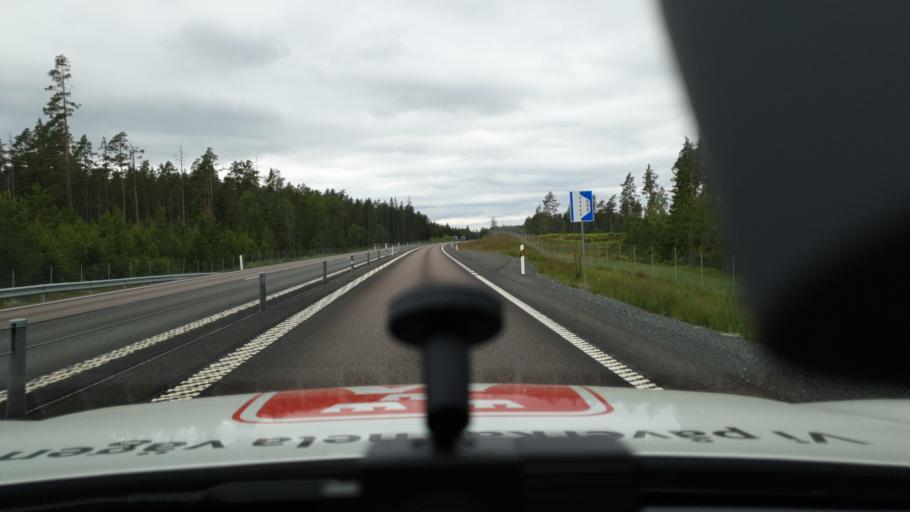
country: SE
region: Joenkoeping
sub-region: Mullsjo Kommun
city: Mullsjoe
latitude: 57.8663
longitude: 13.9706
